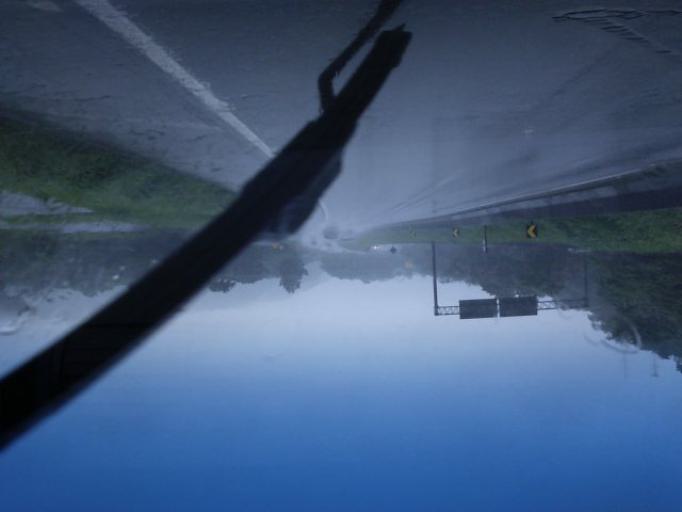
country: BR
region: Parana
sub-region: Guaratuba
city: Guaratuba
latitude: -25.9640
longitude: -48.8976
